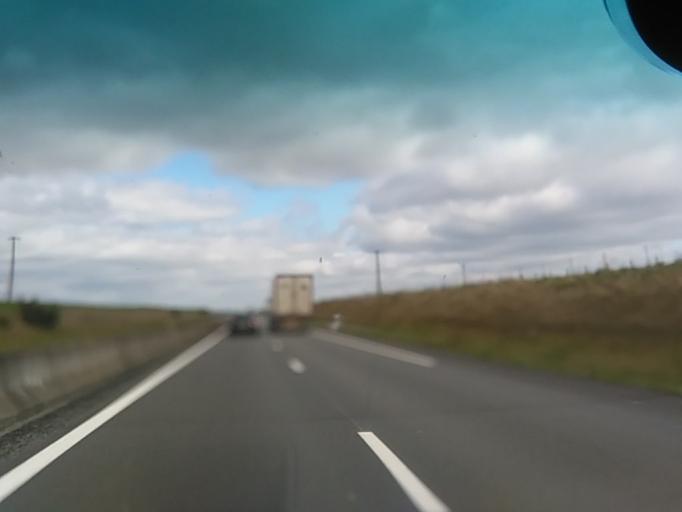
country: FR
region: Haute-Normandie
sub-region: Departement de l'Eure
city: Thiberville
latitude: 49.0953
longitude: 0.4981
